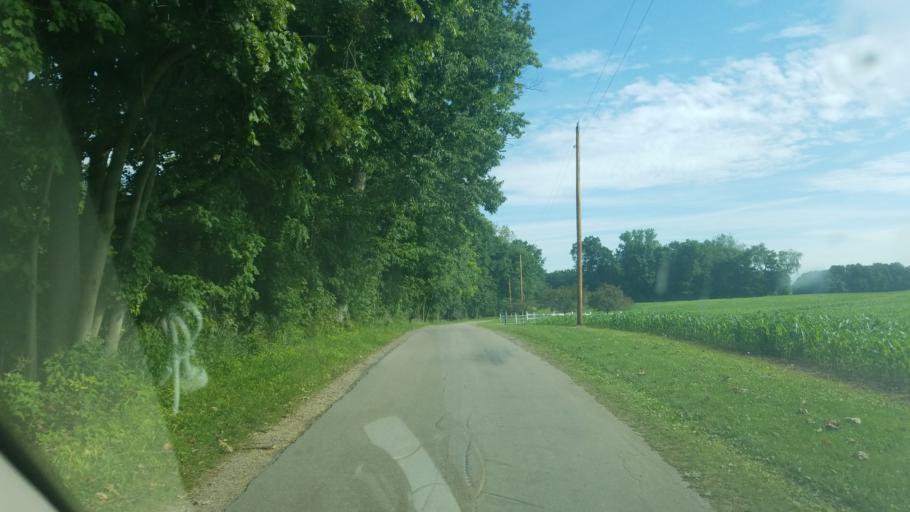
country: US
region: Ohio
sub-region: Wyandot County
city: Upper Sandusky
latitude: 40.7611
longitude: -83.2209
